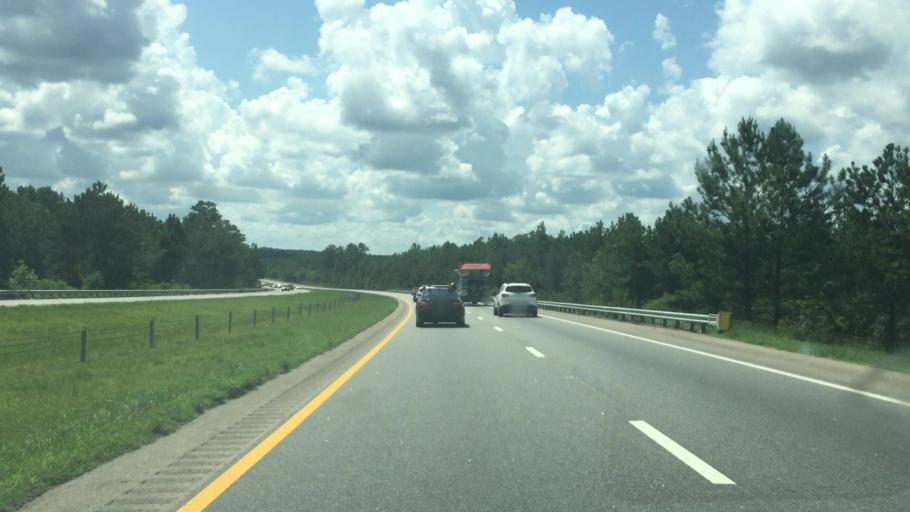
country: US
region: North Carolina
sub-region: Richmond County
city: Cordova
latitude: 34.8930
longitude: -79.7908
